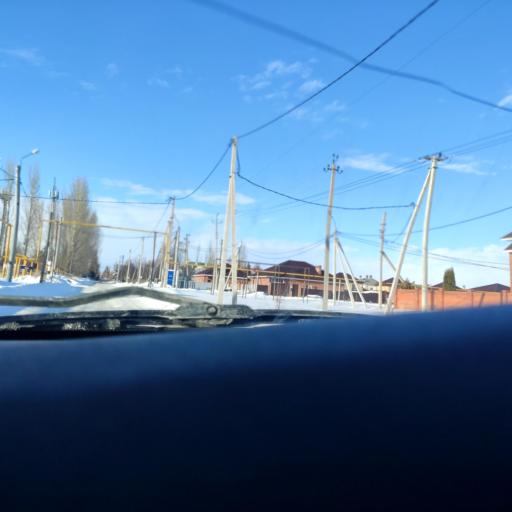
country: RU
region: Samara
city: Podstepki
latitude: 53.5115
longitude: 49.1643
